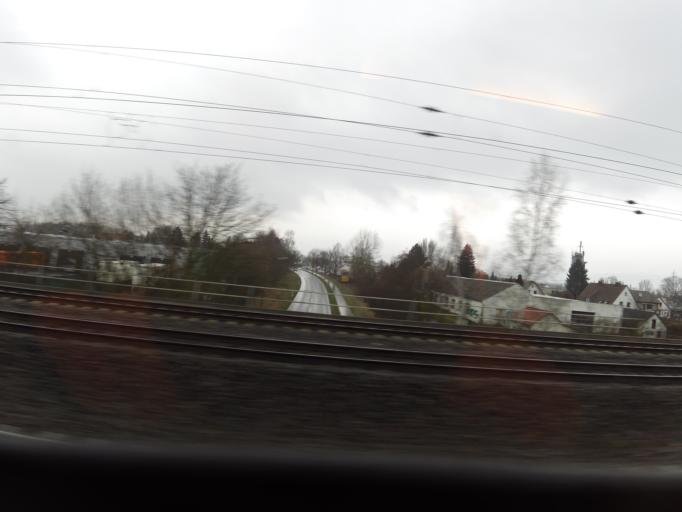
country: DE
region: North Rhine-Westphalia
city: Bad Oeynhausen
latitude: 52.2091
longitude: 8.8411
